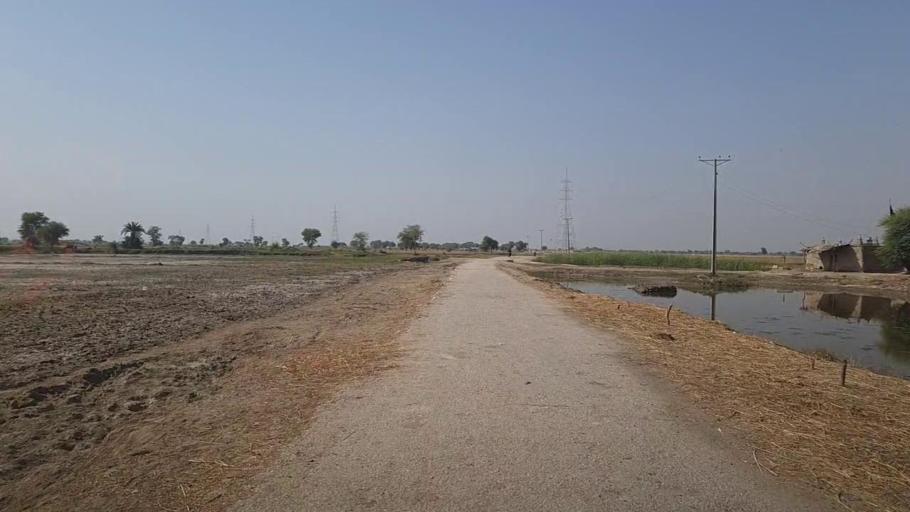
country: PK
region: Sindh
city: Kandhkot
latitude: 28.4095
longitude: 69.2470
